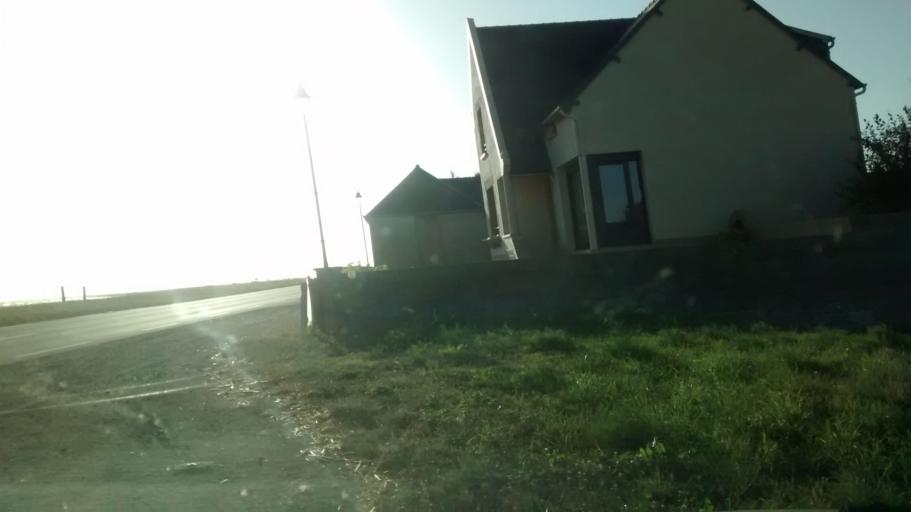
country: FR
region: Brittany
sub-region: Departement d'Ille-et-Vilaine
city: Hirel
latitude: 48.6072
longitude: -1.8053
